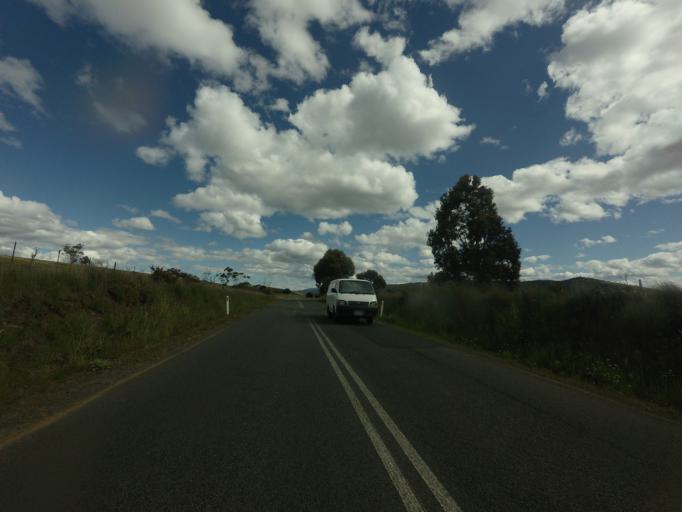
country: AU
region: Tasmania
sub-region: Brighton
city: Bridgewater
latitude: -42.3923
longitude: 147.3148
